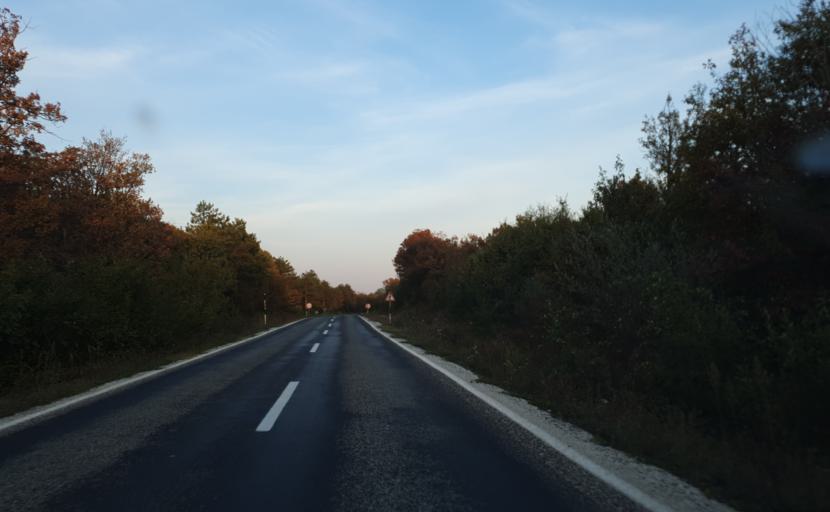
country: TR
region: Kirklareli
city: Igneada
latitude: 41.8674
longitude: 27.8495
